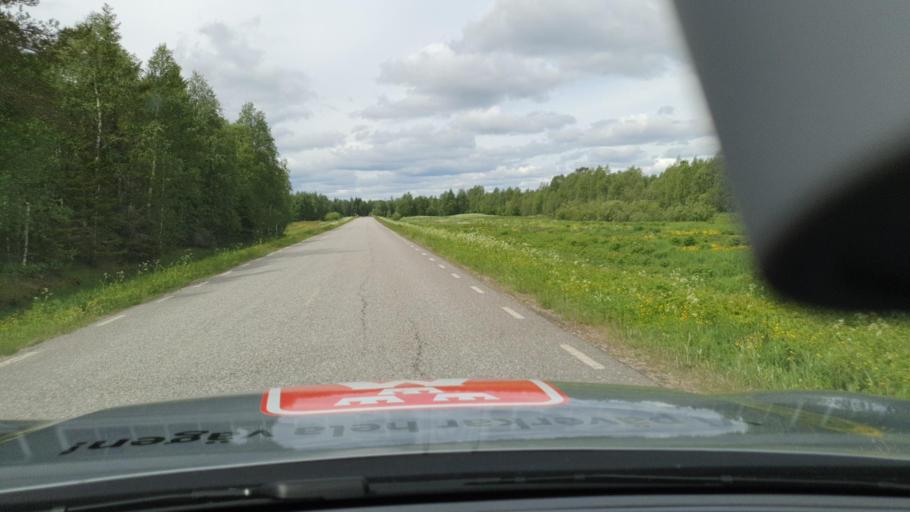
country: FI
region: Lapland
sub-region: Torniolaakso
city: Ylitornio
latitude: 66.0410
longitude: 23.7288
